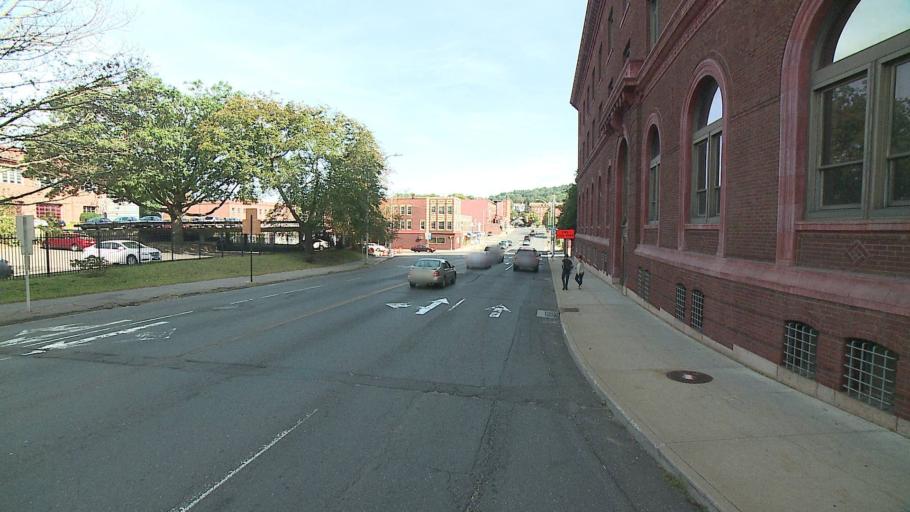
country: US
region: Connecticut
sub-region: New Haven County
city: Waterbury
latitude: 41.5557
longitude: -73.0464
